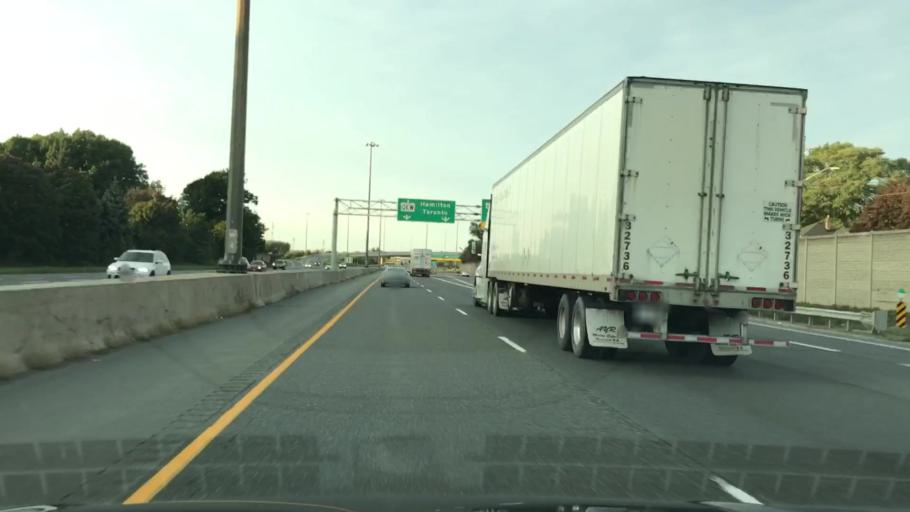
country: CA
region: Ontario
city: Niagara Falls
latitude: 43.0910
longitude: -79.1189
